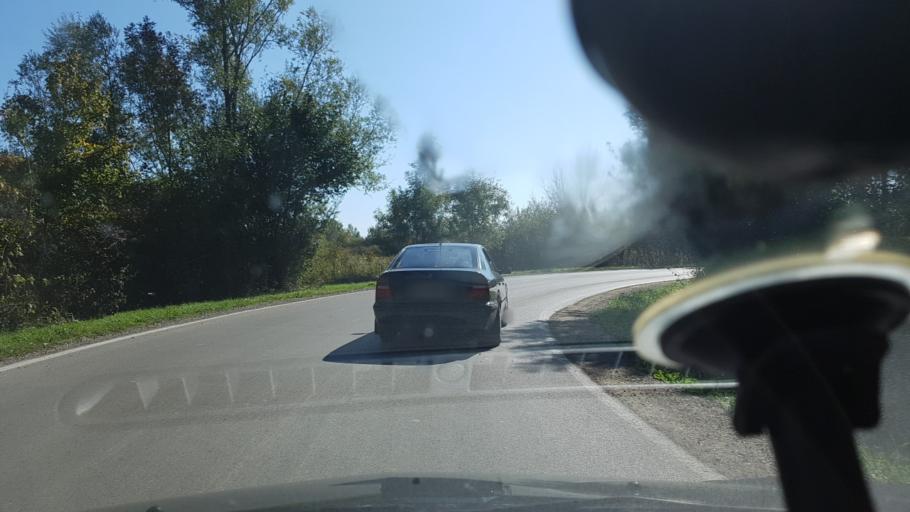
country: HR
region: Zagrebacka
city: Lupoglav
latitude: 45.7285
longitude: 16.3039
